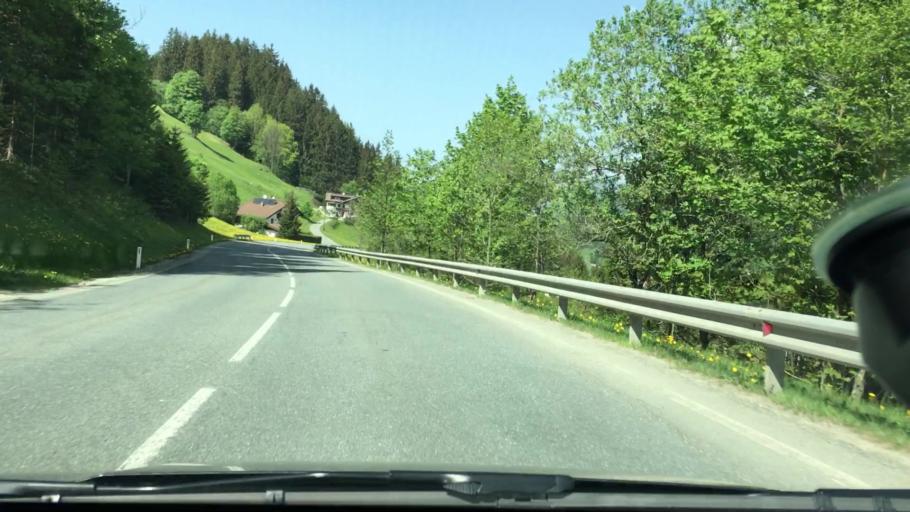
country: AT
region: Tyrol
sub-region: Politischer Bezirk Kitzbuhel
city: Jochberg
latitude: 47.3485
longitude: 12.4126
